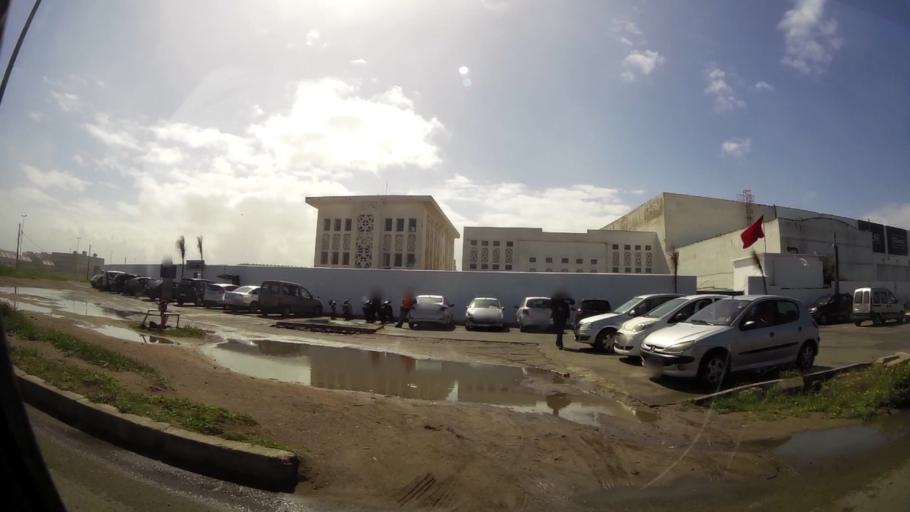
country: MA
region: Grand Casablanca
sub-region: Mediouna
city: Tit Mellil
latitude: 33.6279
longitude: -7.5173
